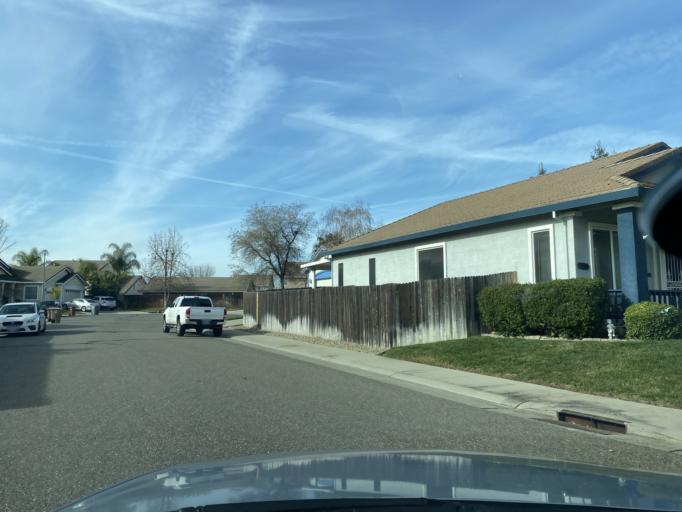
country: US
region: California
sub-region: Sacramento County
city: Elk Grove
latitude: 38.4443
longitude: -121.3827
